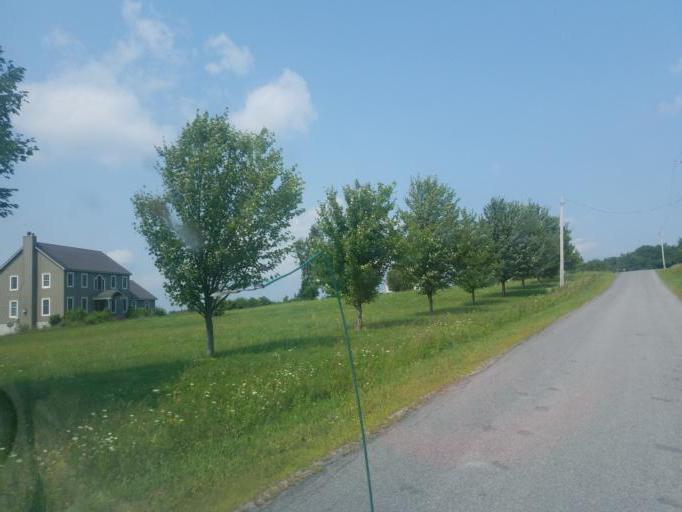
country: US
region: New York
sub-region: Montgomery County
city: Wellsville
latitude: 42.8644
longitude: -74.3269
